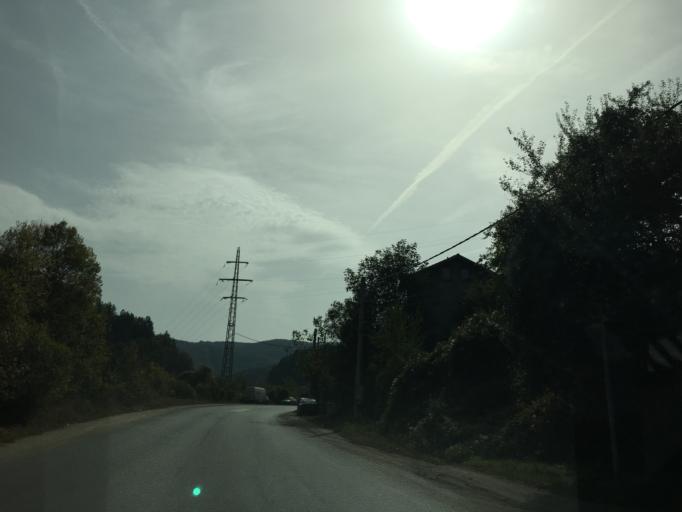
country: BG
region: Sofia-Capital
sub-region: Stolichna Obshtina
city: Sofia
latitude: 42.5820
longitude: 23.4246
